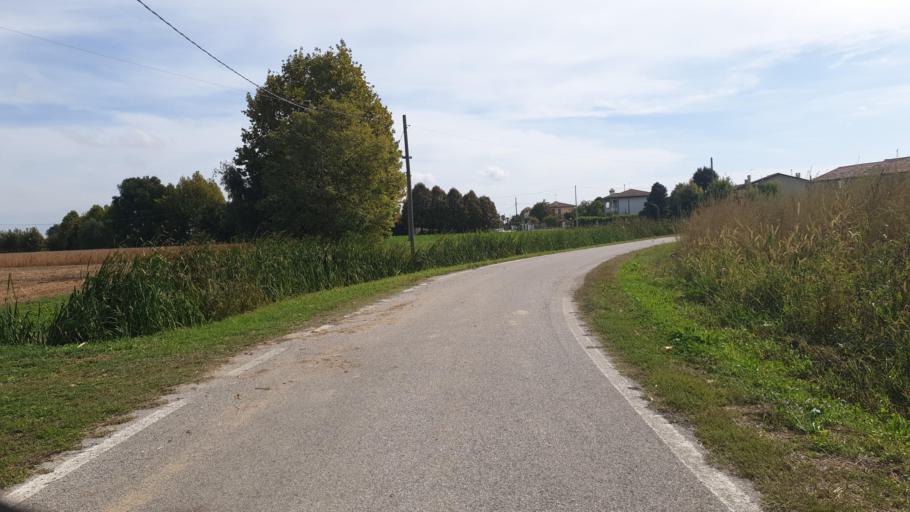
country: IT
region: Veneto
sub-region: Provincia di Padova
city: Brugine
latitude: 45.2973
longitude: 11.9737
